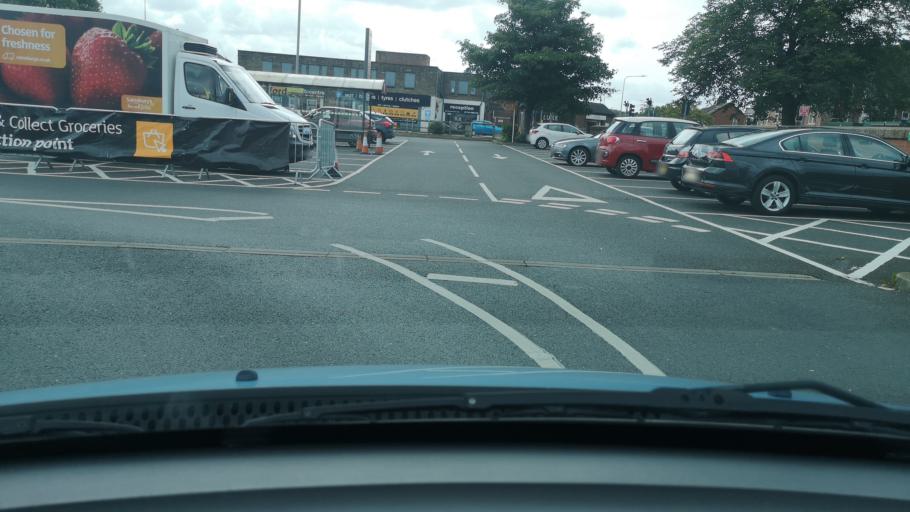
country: GB
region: England
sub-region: North Lincolnshire
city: Scunthorpe
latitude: 53.5912
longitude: -0.6608
